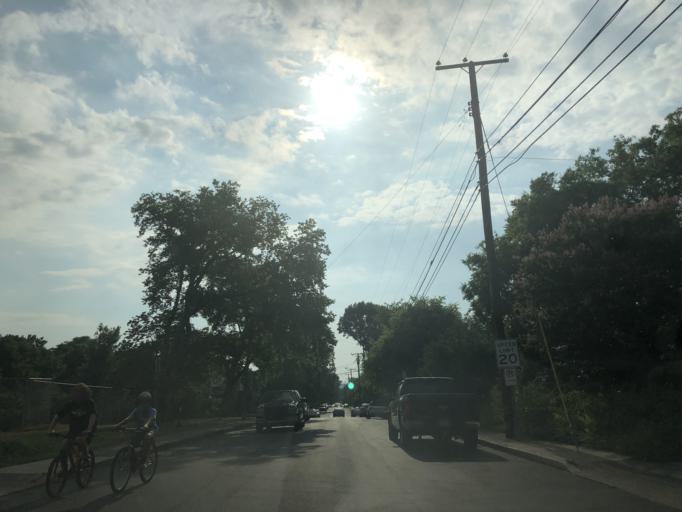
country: US
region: Tennessee
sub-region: Davidson County
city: Nashville
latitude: 36.1276
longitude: -86.8040
